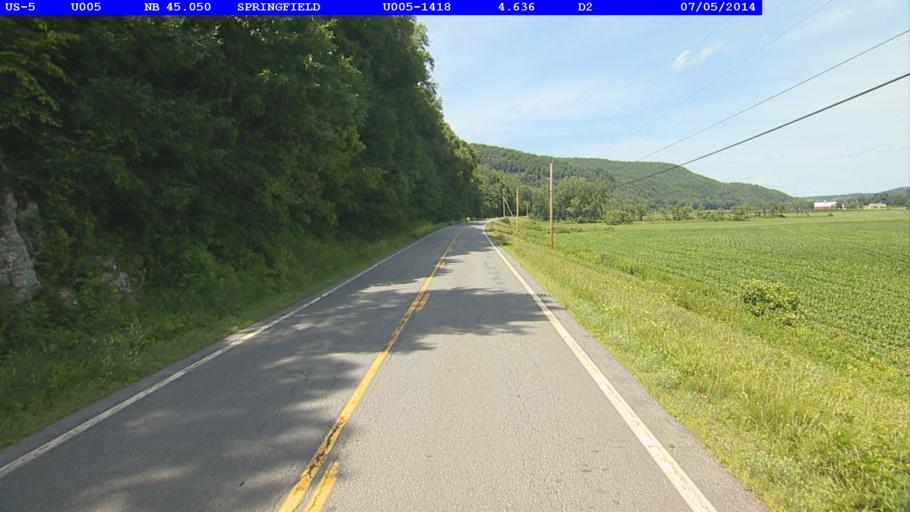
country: US
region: New Hampshire
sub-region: Sullivan County
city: Charlestown
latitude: 43.2806
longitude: -72.4135
